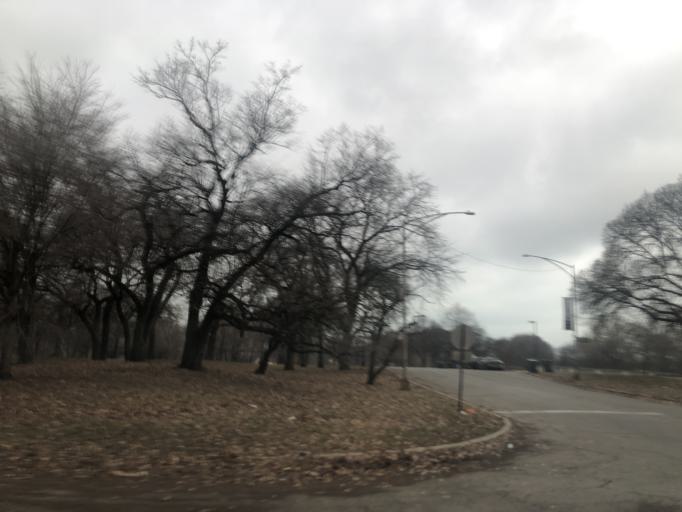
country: US
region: Illinois
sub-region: Cook County
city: Chicago
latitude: 41.7917
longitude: -87.6082
